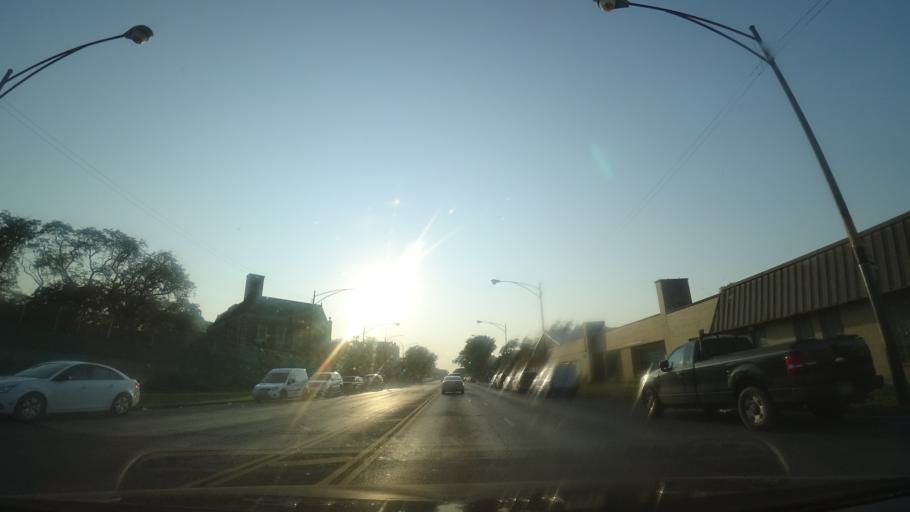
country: US
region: Illinois
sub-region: Cook County
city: Elmwood Park
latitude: 41.9237
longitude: -87.7795
